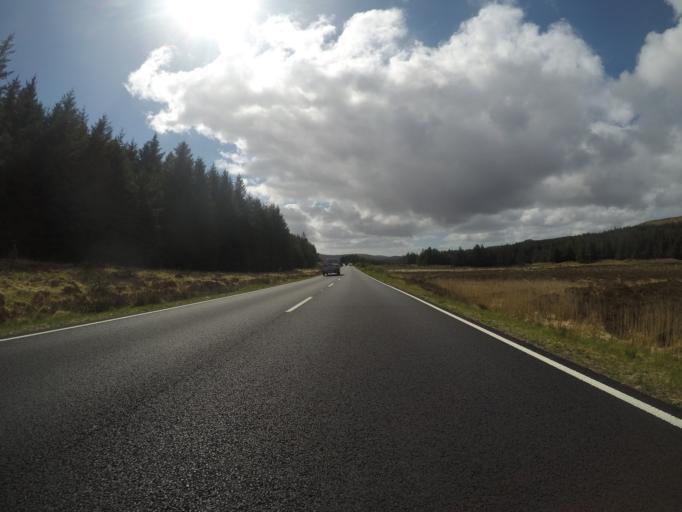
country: GB
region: Scotland
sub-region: Highland
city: Isle of Skye
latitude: 57.3318
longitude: -6.2008
